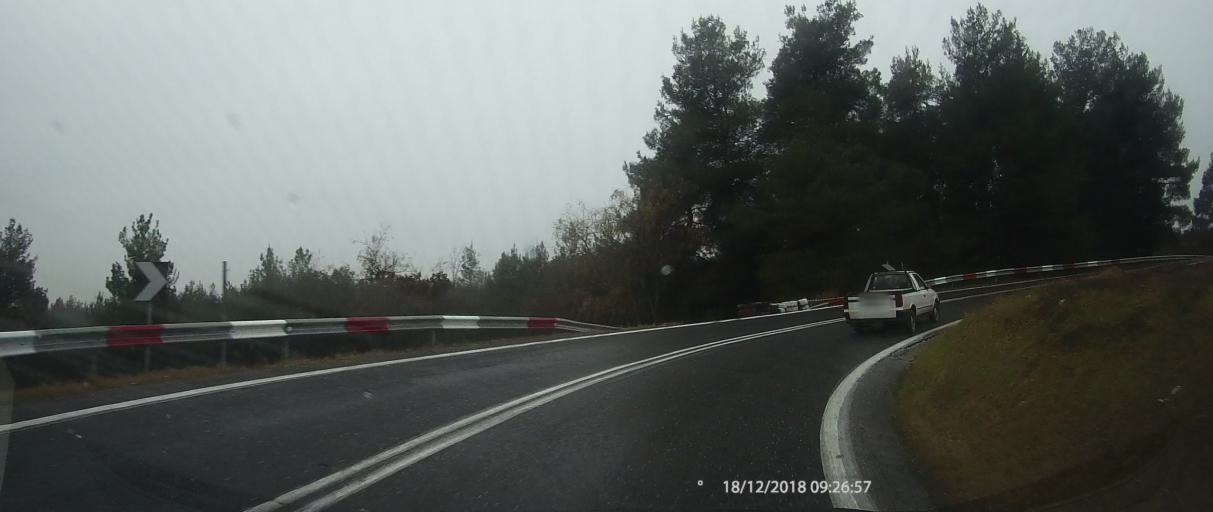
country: GR
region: Thessaly
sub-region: Nomos Larisis
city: Elassona
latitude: 39.9155
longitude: 22.1809
